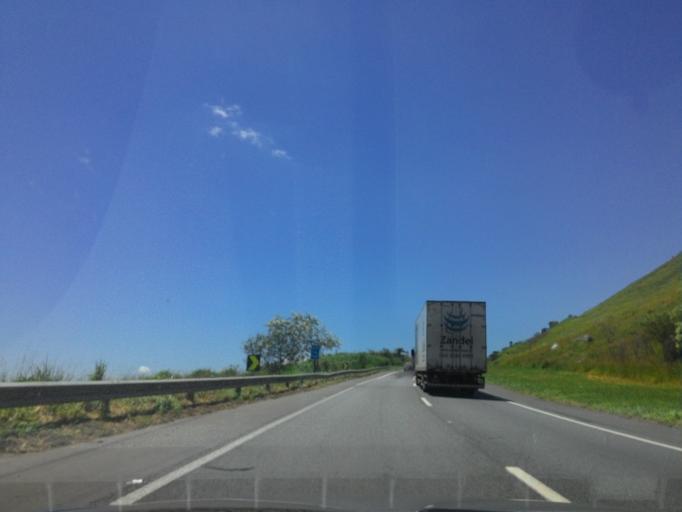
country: BR
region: Sao Paulo
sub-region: Cajati
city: Cajati
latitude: -24.9702
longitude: -48.4883
